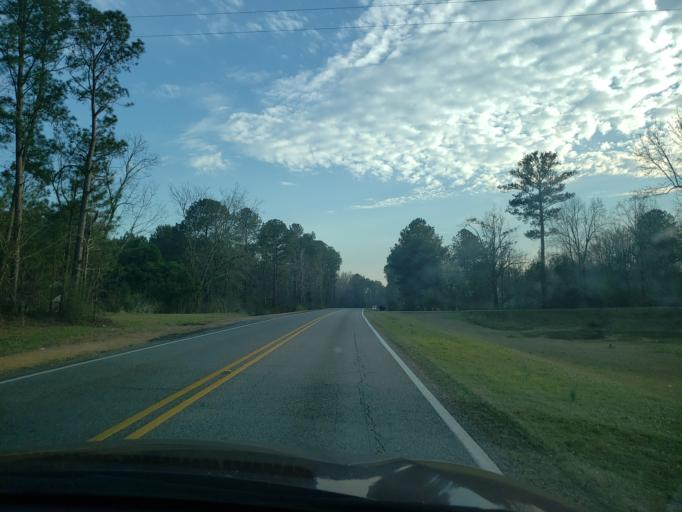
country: US
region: Alabama
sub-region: Hale County
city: Greensboro
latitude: 32.7328
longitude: -87.5867
